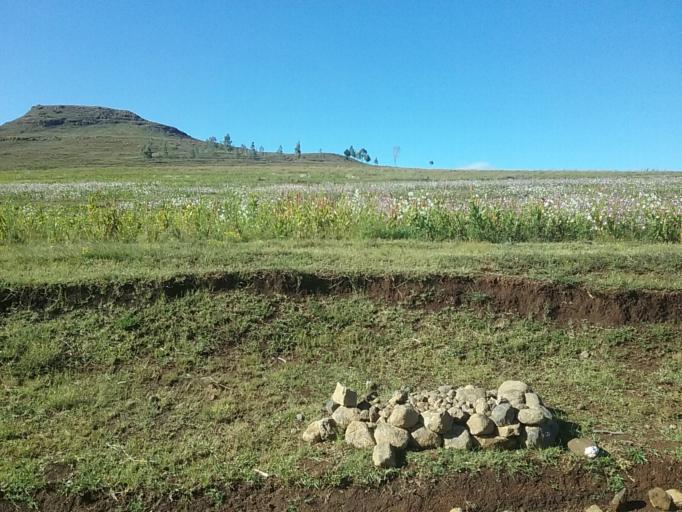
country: LS
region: Berea
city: Teyateyaneng
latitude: -29.2158
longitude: 27.8610
